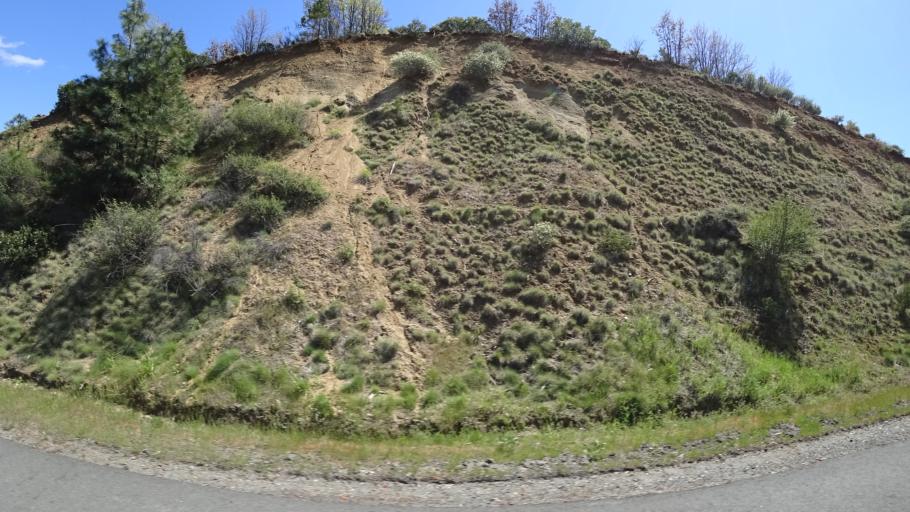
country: US
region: California
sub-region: Trinity County
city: Weaverville
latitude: 40.7363
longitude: -122.9514
